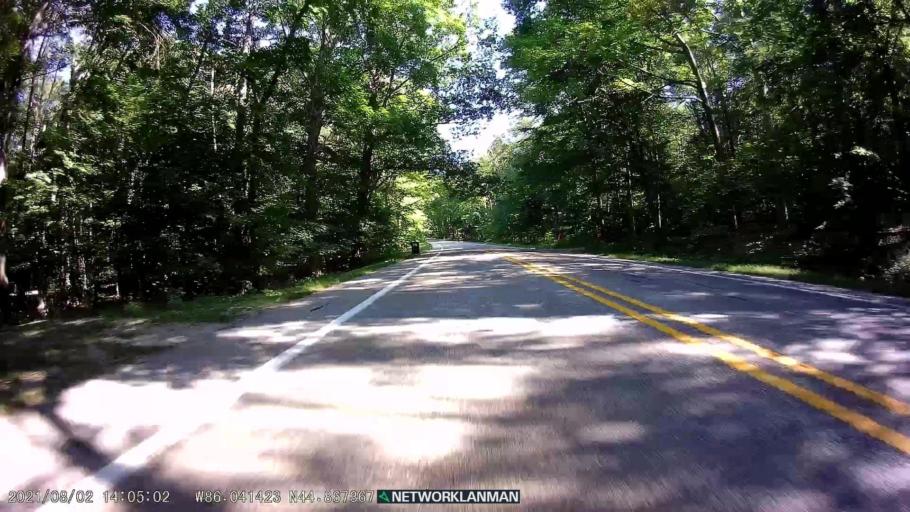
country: US
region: Michigan
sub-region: Benzie County
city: Beulah
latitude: 44.8676
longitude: -86.0417
